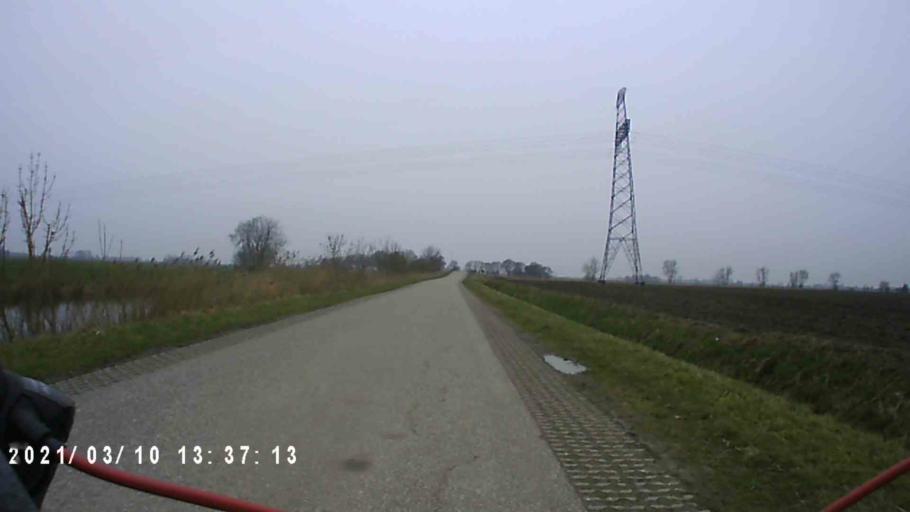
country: NL
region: Groningen
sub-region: Gemeente Winsum
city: Winsum
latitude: 53.3328
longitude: 6.4979
